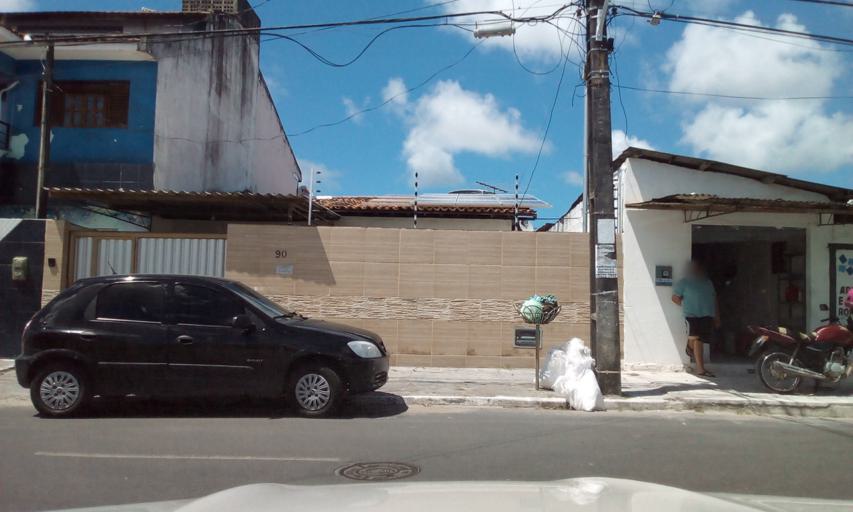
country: BR
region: Paraiba
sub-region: Joao Pessoa
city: Joao Pessoa
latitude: -7.1733
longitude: -34.8612
